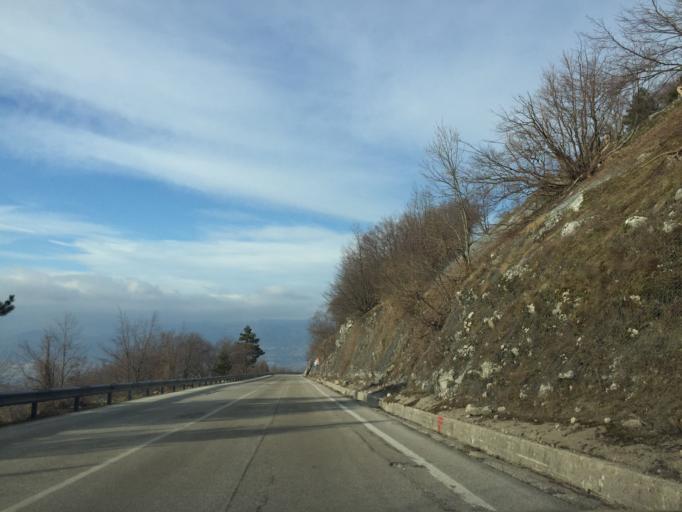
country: IT
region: Molise
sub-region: Provincia di Campobasso
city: San Massimo
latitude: 41.4721
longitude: 14.4114
